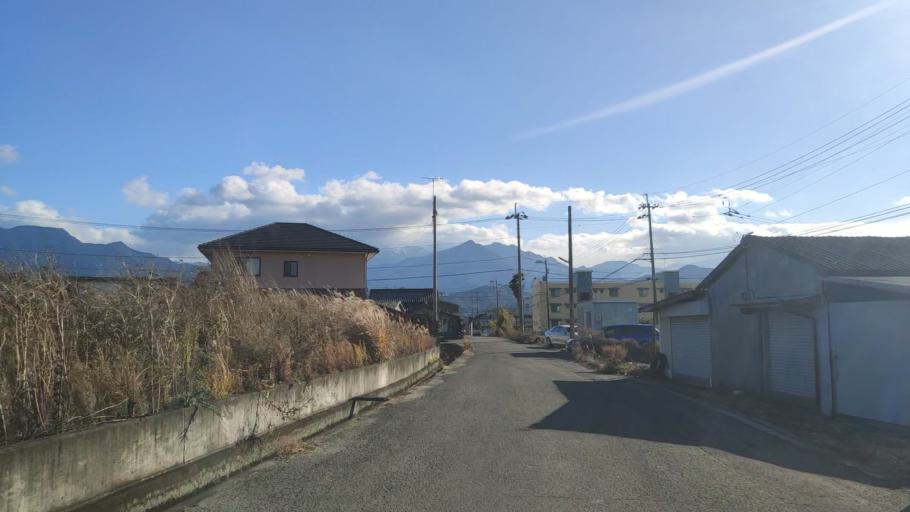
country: JP
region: Ehime
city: Saijo
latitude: 33.9215
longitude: 133.1620
